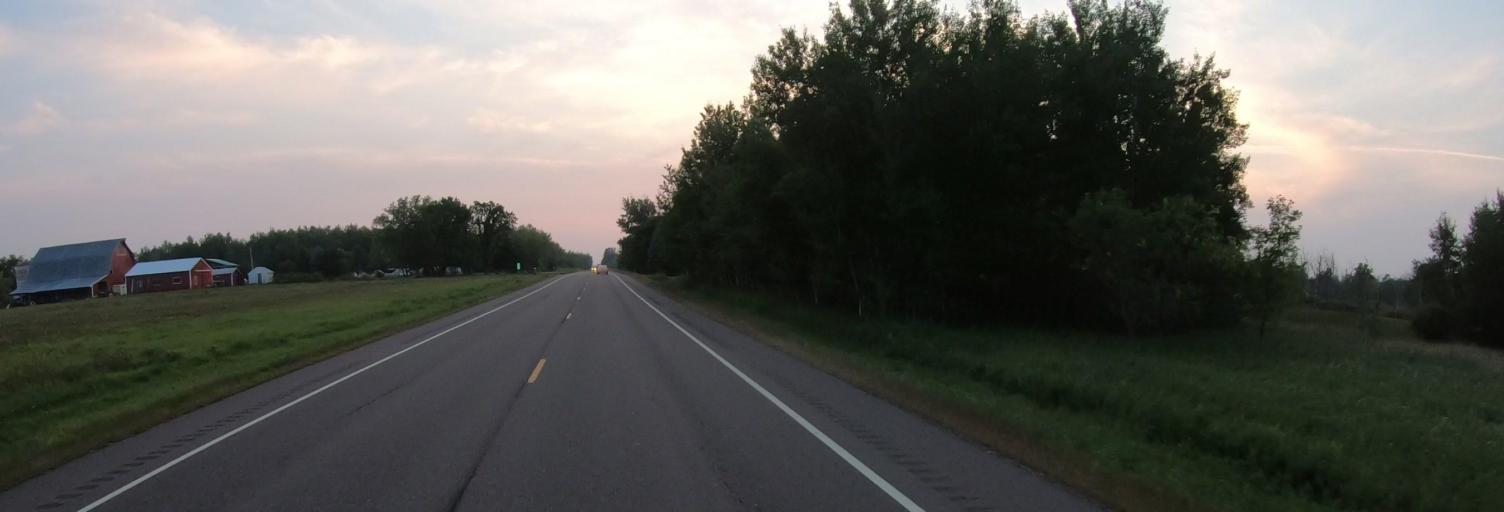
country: US
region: Minnesota
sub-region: Pine County
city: Rock Creek
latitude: 45.7735
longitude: -92.8700
